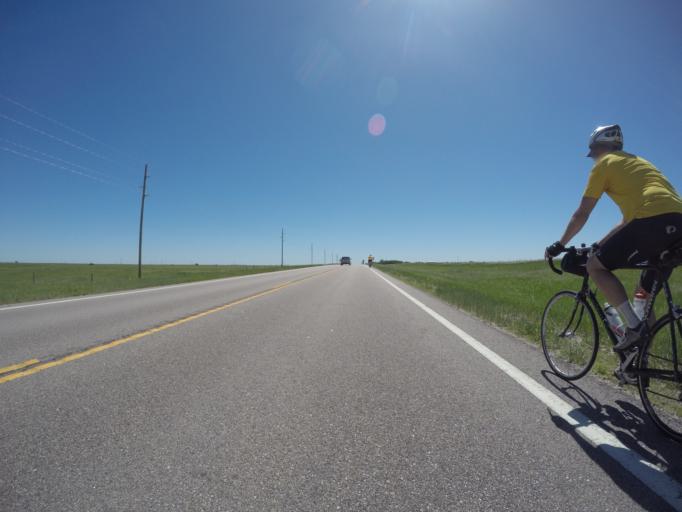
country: US
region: Kansas
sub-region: Norton County
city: Norton
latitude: 39.8283
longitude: -99.6884
